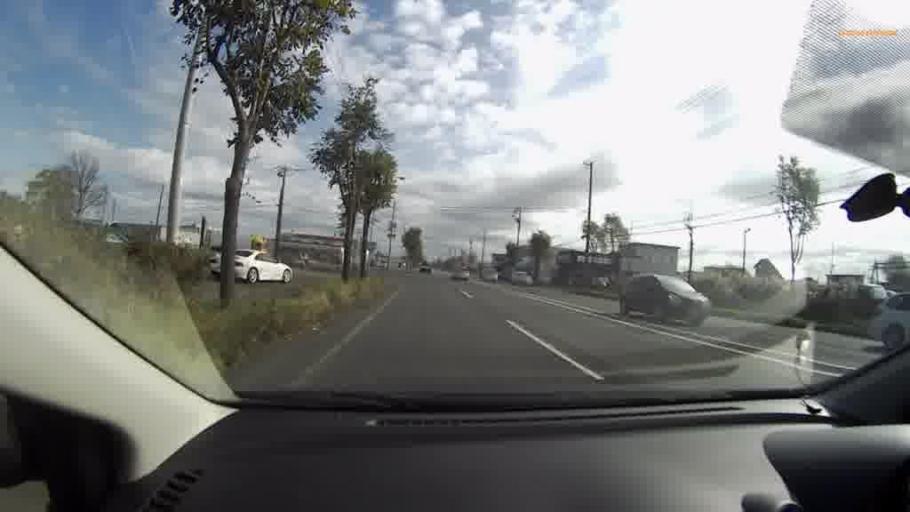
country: JP
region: Hokkaido
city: Kushiro
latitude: 43.0118
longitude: 144.2999
